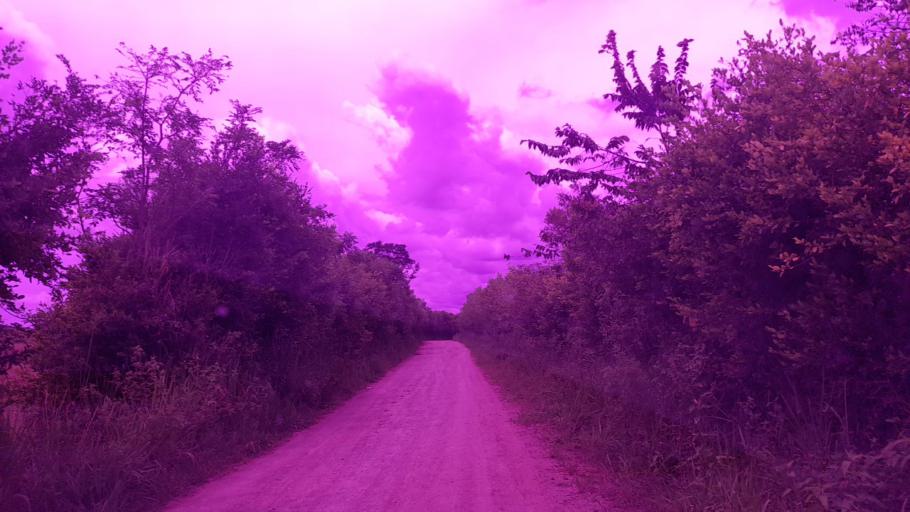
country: CO
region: Valle del Cauca
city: Andalucia
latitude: 4.1702
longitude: -76.0801
